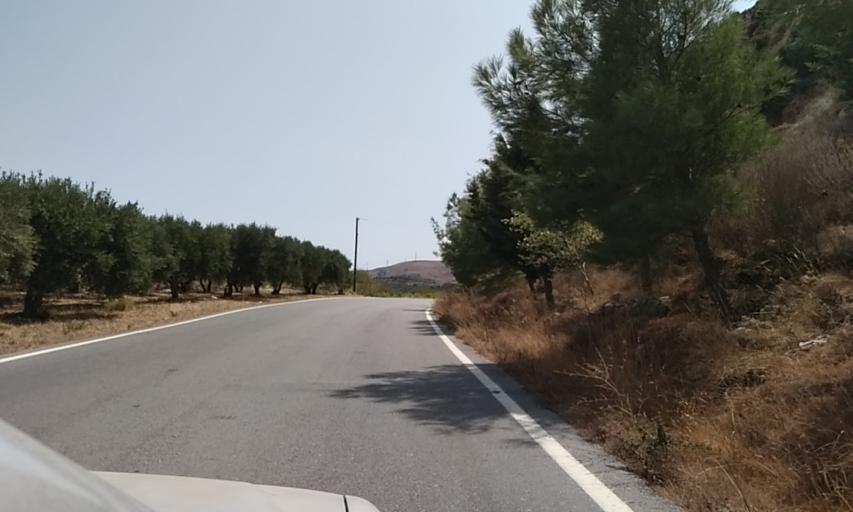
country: GR
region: Crete
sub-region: Nomos Lasithiou
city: Siteia
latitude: 35.1085
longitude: 26.0584
